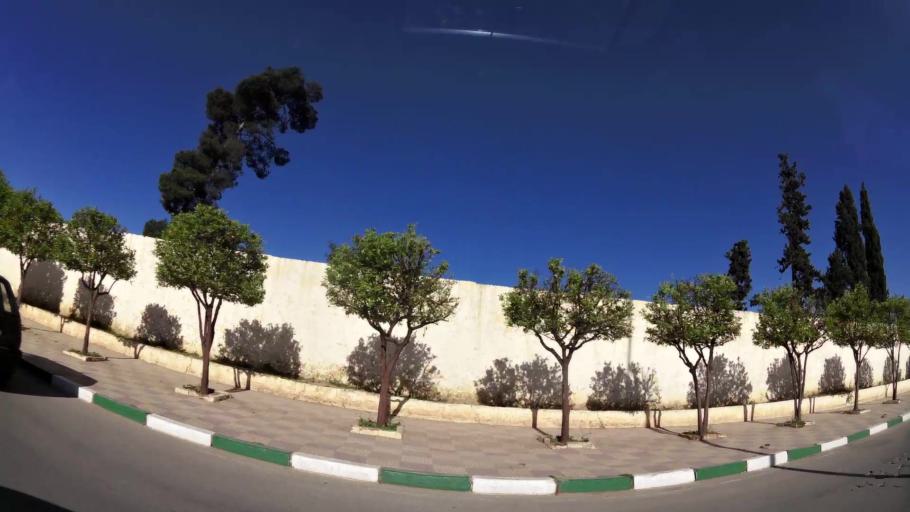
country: MA
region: Meknes-Tafilalet
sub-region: Meknes
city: Meknes
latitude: 33.8773
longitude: -5.5739
